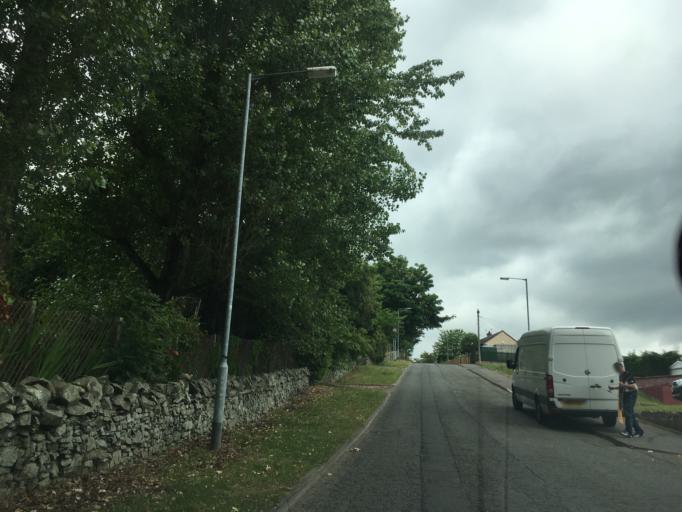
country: GB
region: Scotland
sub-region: The Scottish Borders
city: Peebles
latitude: 55.6434
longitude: -3.1847
